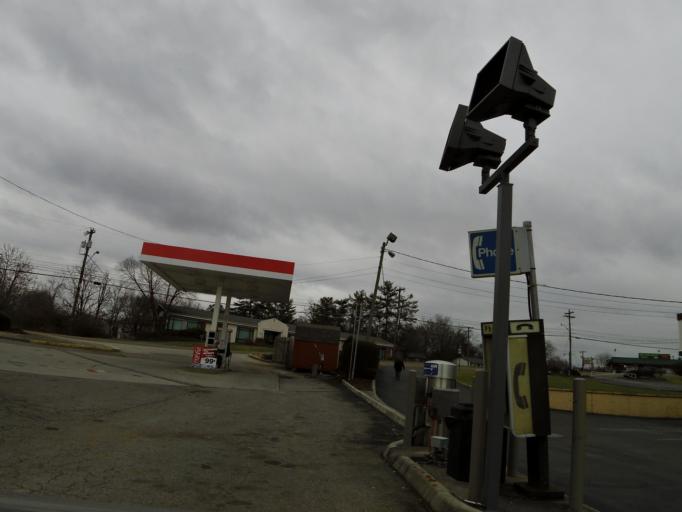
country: US
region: Tennessee
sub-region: Hamblen County
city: Morristown
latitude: 36.2044
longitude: -83.3068
